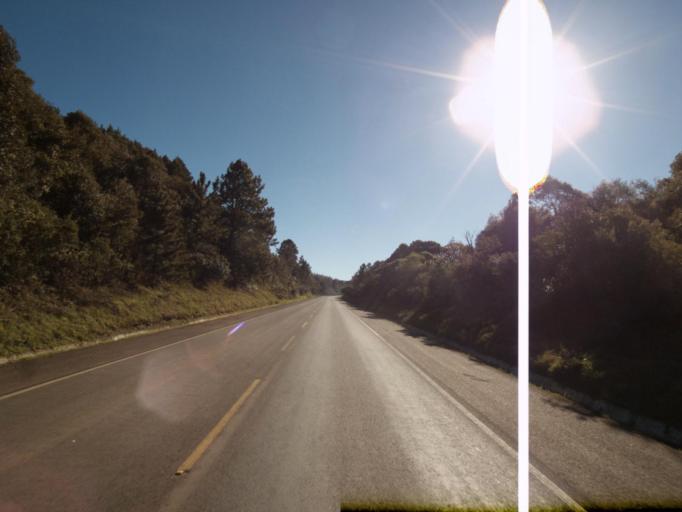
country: BR
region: Santa Catarina
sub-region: Concordia
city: Concordia
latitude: -26.9276
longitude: -51.8113
